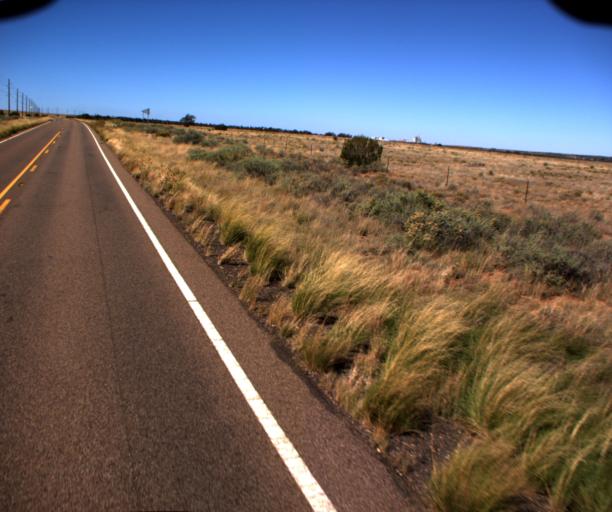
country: US
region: Arizona
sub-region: Navajo County
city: Taylor
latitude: 34.4829
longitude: -110.2864
